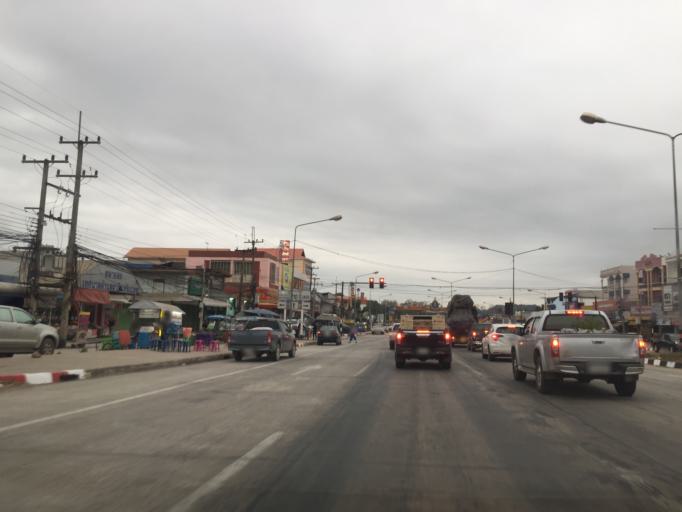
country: TH
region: Loei
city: Erawan
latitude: 17.3012
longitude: 101.9555
